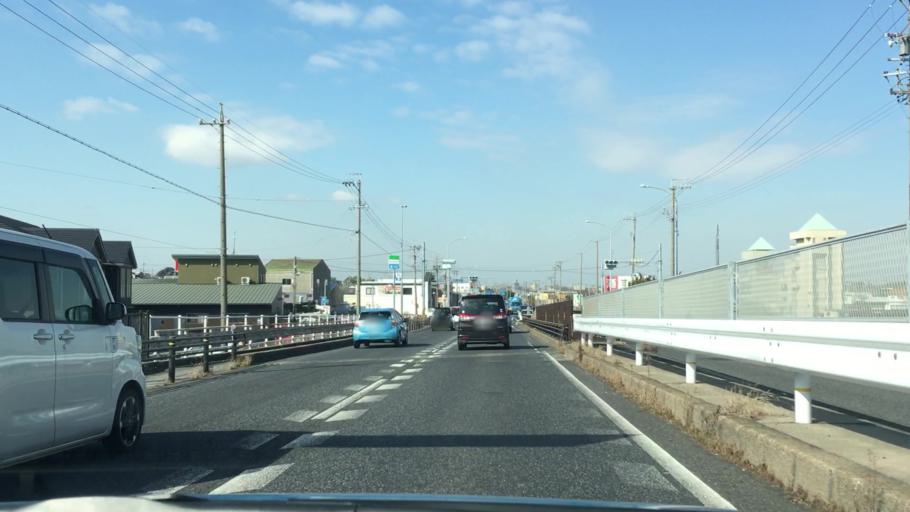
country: JP
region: Aichi
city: Okazaki
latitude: 34.9249
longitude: 137.2022
